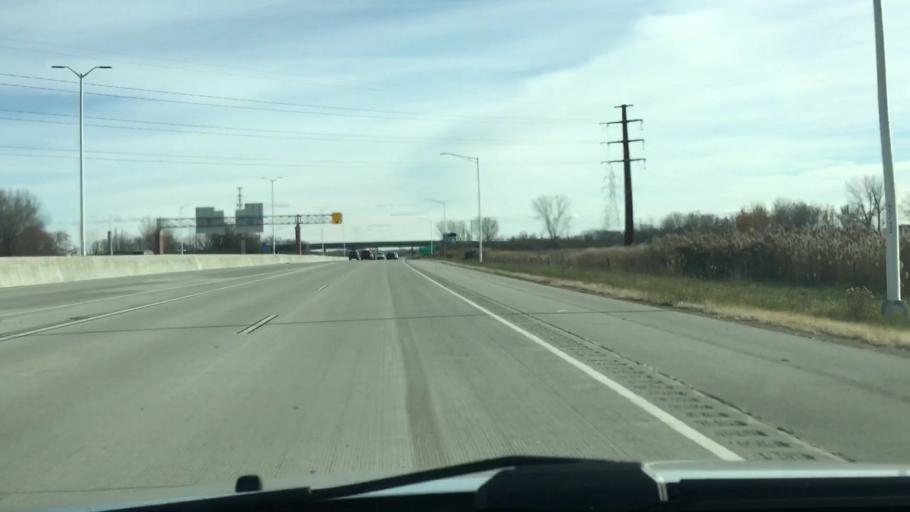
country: US
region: Wisconsin
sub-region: Brown County
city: Howard
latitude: 44.5549
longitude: -88.0460
